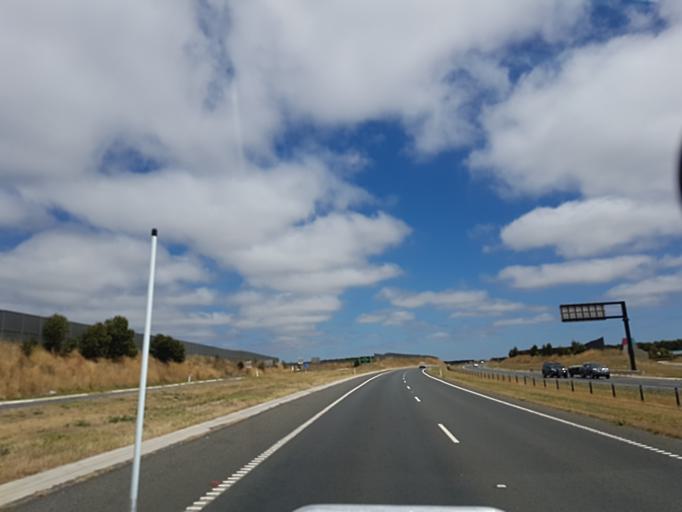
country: AU
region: Victoria
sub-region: Greater Geelong
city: Wandana Heights
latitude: -38.2178
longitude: 144.2696
